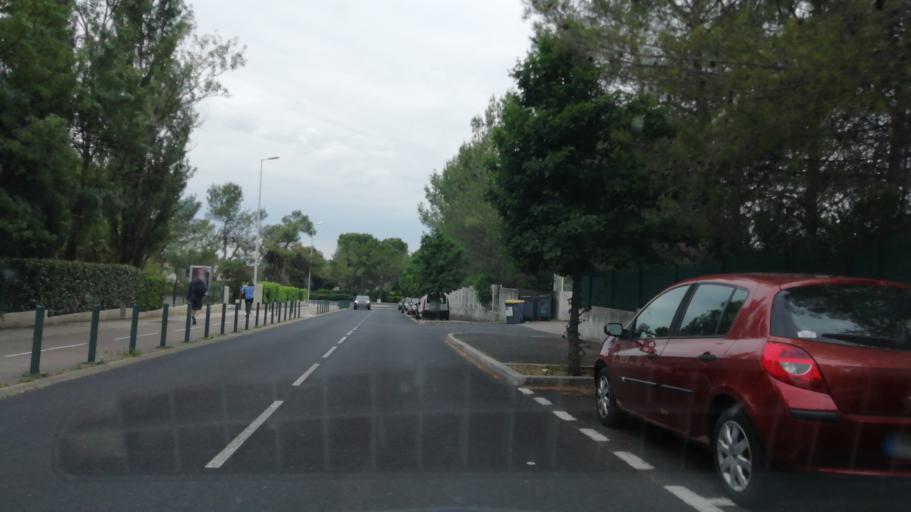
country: FR
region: Languedoc-Roussillon
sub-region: Departement de l'Herault
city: Saint-Clement-de-Riviere
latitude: 43.7100
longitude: 3.8325
